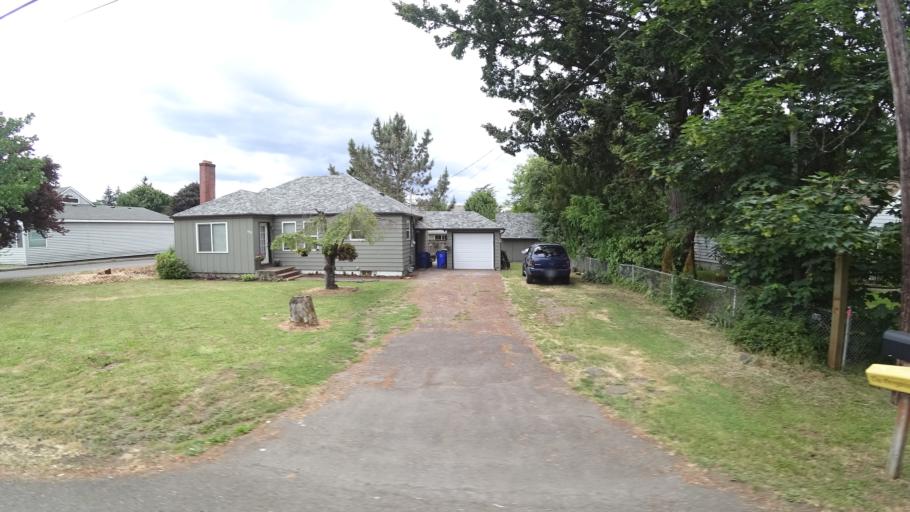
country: US
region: Oregon
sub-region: Clackamas County
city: Happy Valley
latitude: 45.4979
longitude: -122.5145
